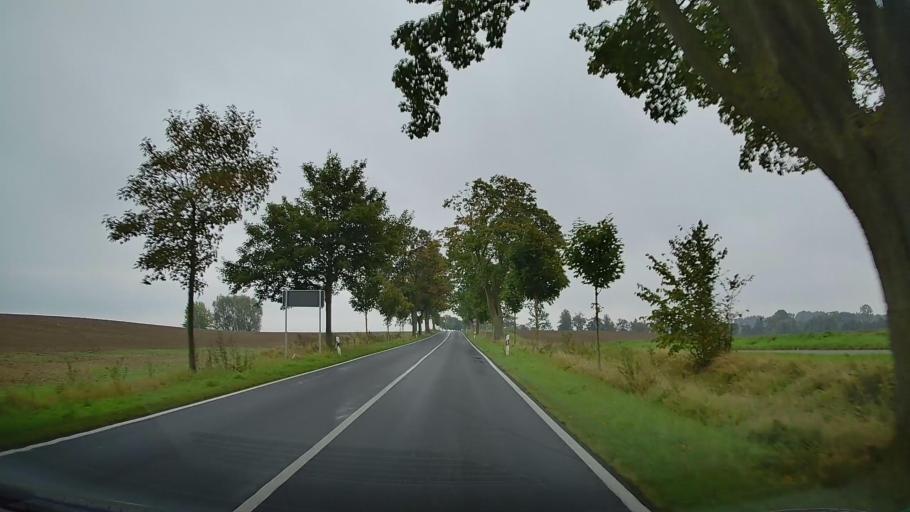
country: DE
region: Mecklenburg-Vorpommern
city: Ostseebad Boltenhagen
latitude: 53.9536
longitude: 11.2265
